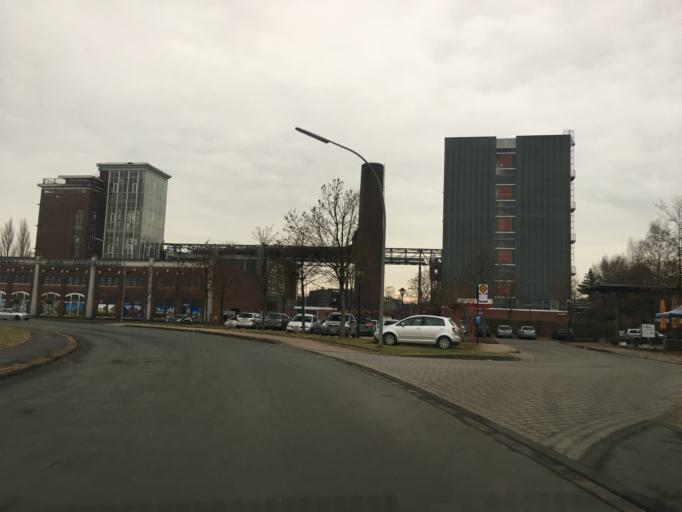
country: DE
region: North Rhine-Westphalia
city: Ludinghausen
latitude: 51.7626
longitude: 7.4319
